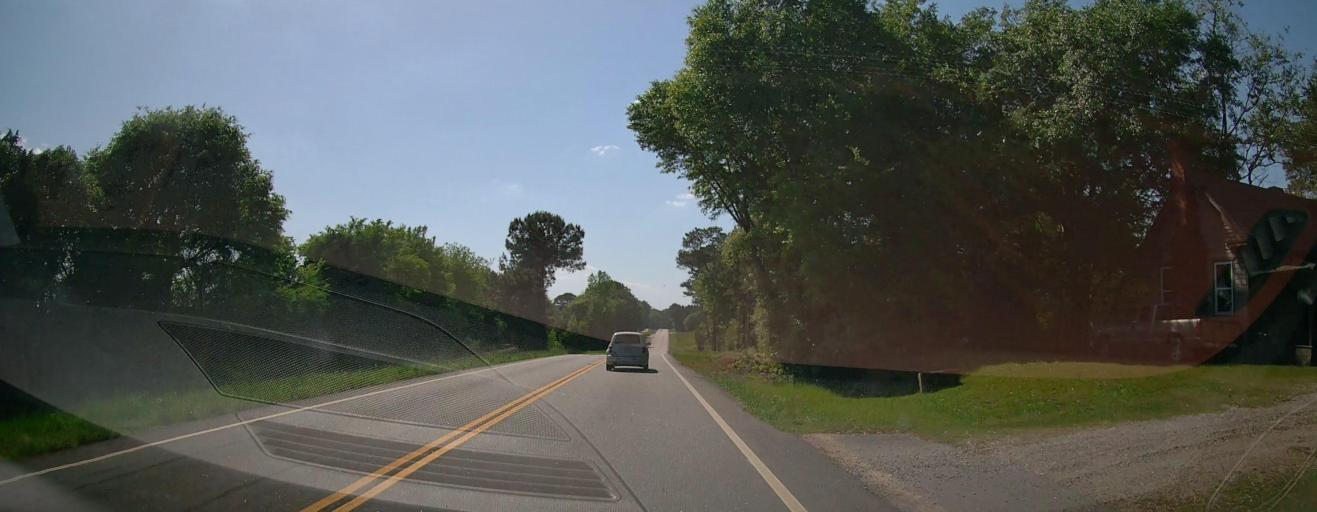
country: US
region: Georgia
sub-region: Morgan County
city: Madison
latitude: 33.5987
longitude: -83.4101
